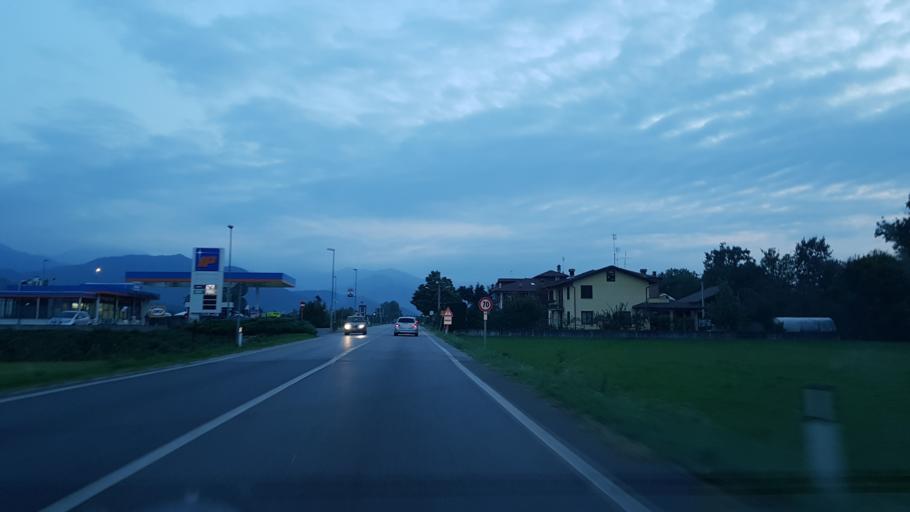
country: IT
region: Piedmont
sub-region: Provincia di Cuneo
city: Mondovi
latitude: 44.3674
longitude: 7.7977
